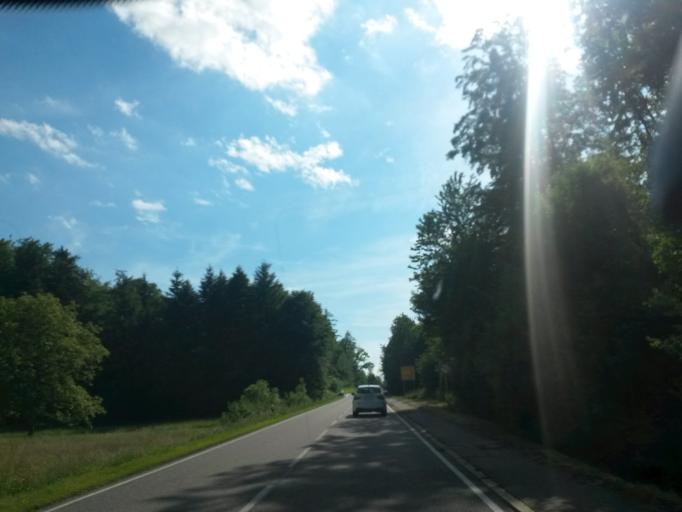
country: DE
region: Baden-Wuerttemberg
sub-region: Regierungsbezirk Stuttgart
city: Renningen
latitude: 48.7511
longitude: 8.9150
